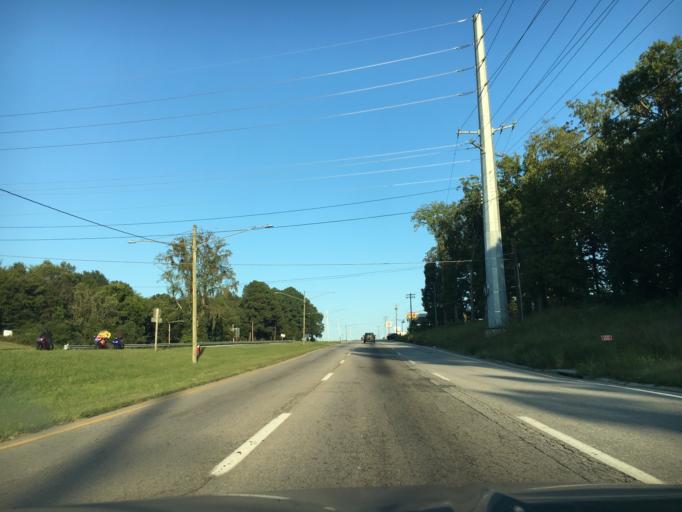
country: US
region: Virginia
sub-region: City of Danville
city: Danville
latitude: 36.5822
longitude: -79.3512
